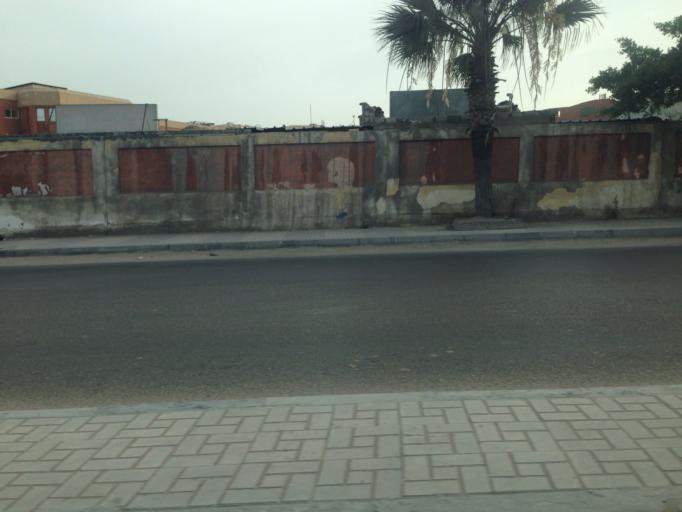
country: EG
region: Alexandria
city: Alexandria
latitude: 31.2066
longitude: 29.9671
